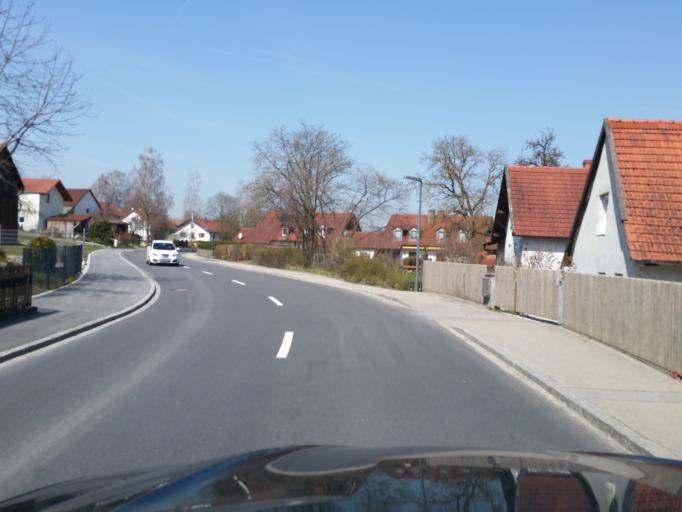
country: DE
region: Bavaria
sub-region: Upper Bavaria
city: Kirchberg
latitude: 48.4518
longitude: 12.0272
